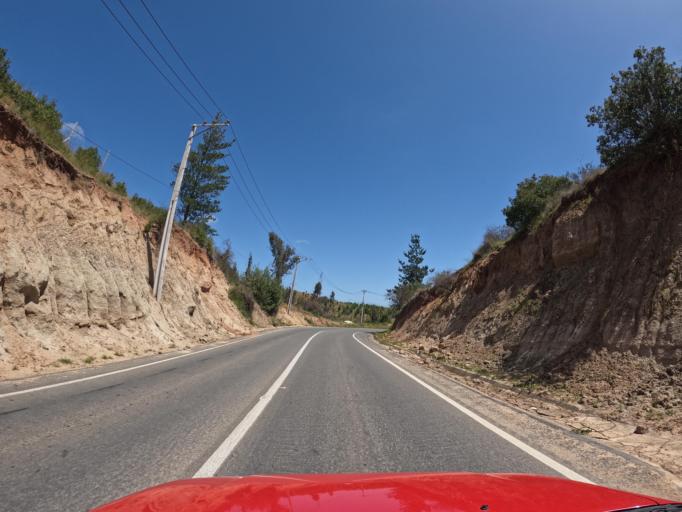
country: CL
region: O'Higgins
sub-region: Provincia de Colchagua
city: Santa Cruz
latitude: -34.6621
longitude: -71.8467
